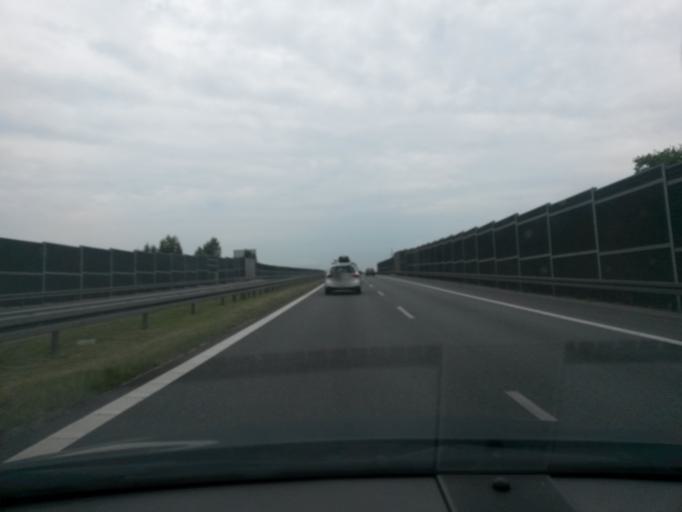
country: PL
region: Masovian Voivodeship
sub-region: Powiat zyrardowski
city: Mszczonow
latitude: 51.9716
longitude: 20.5030
